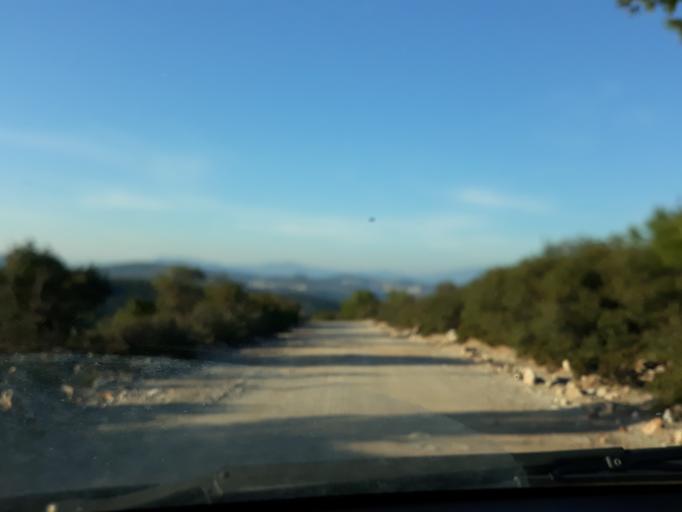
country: GR
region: Central Greece
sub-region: Nomos Voiotias
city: Asopia
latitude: 38.2484
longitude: 23.5322
